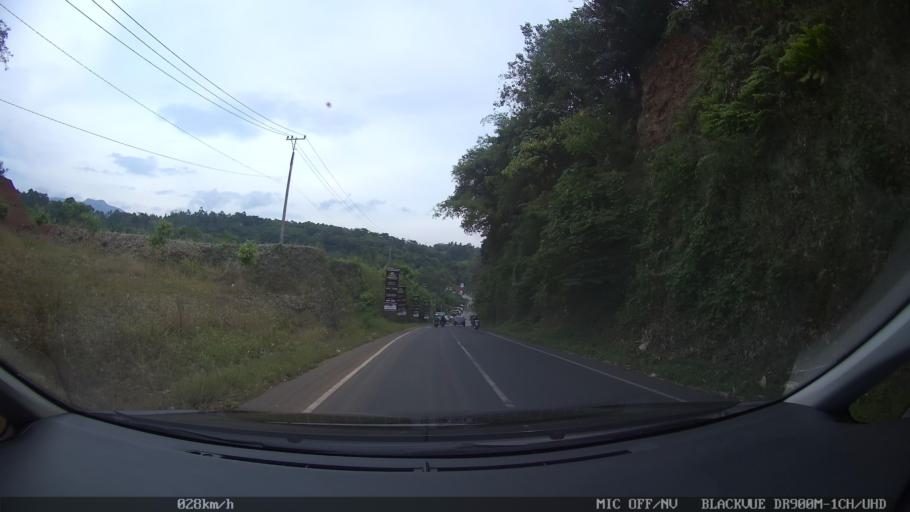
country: ID
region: Lampung
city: Bandarlampung
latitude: -5.4145
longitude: 105.2288
